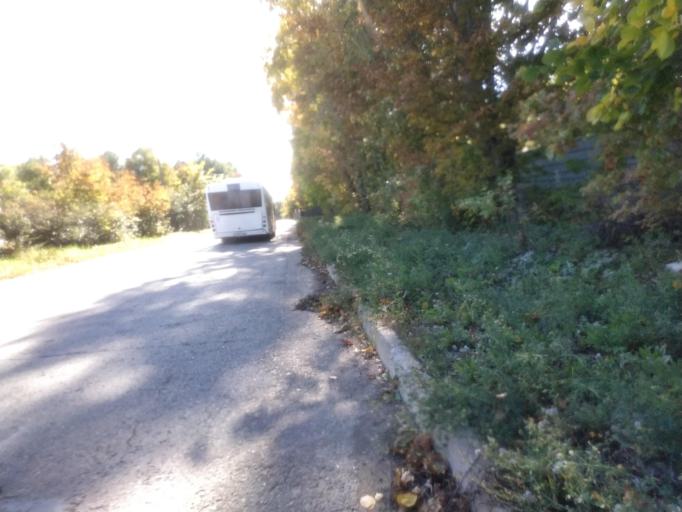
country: RU
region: Chuvashia
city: Novyye Lapsary
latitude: 56.1405
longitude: 47.1415
